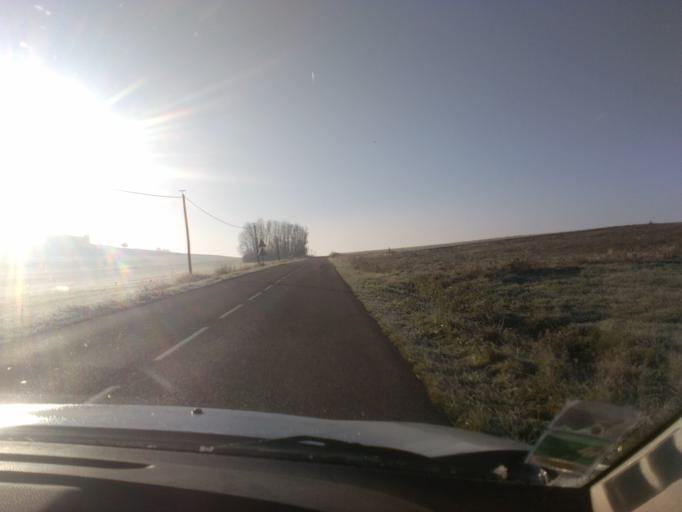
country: FR
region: Lorraine
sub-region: Departement des Vosges
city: Darnieulles
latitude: 48.1564
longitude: 6.2356
